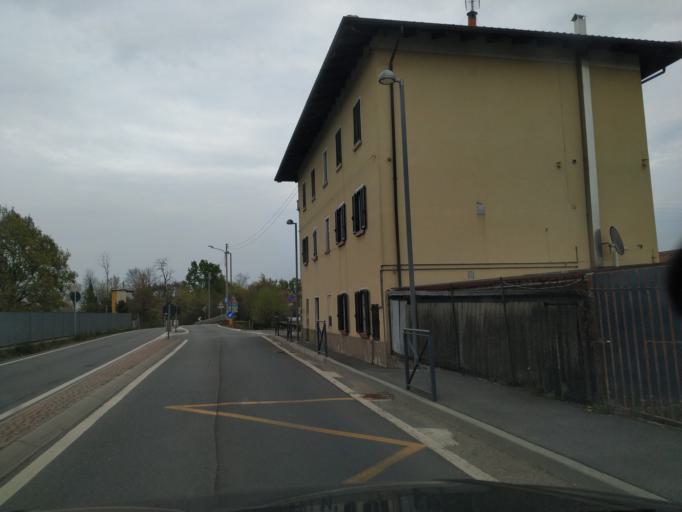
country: IT
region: Piedmont
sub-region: Provincia di Novara
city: Cureggio
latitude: 45.6660
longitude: 8.4442
